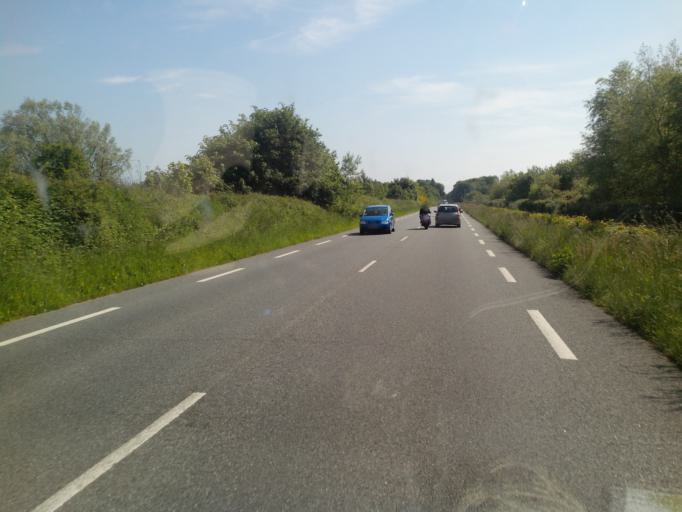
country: FR
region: Picardie
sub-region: Departement de la Somme
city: Quend
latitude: 50.3569
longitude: 1.6505
